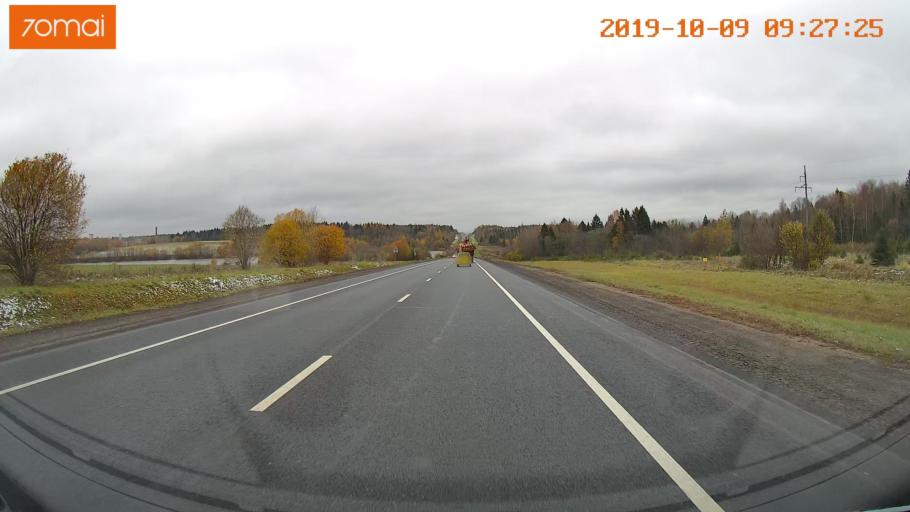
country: RU
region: Vologda
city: Vologda
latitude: 59.1126
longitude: 39.9787
